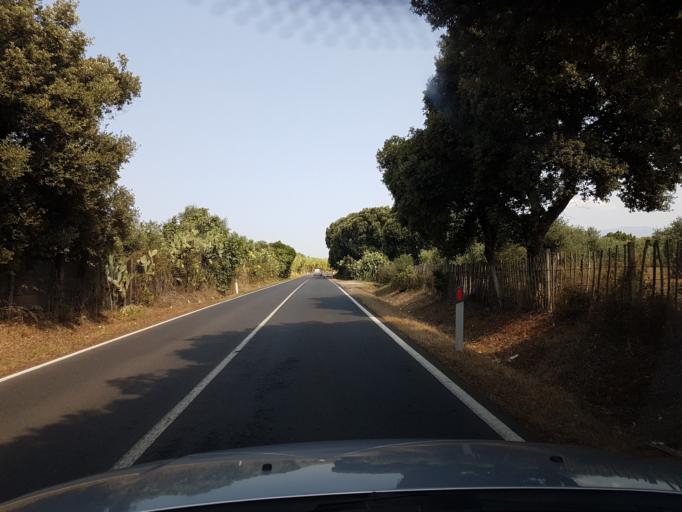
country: IT
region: Sardinia
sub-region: Provincia di Oristano
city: Donigala Fenugheddu
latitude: 39.9394
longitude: 8.5710
